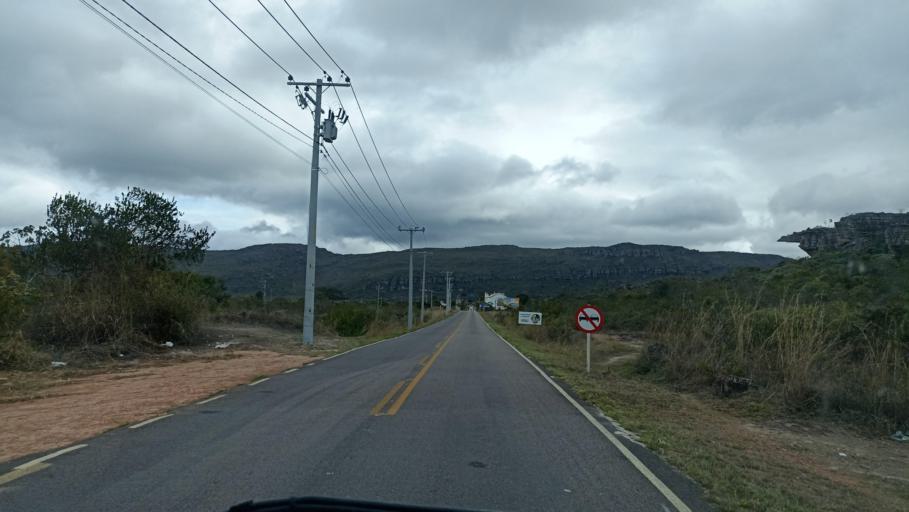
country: BR
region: Bahia
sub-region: Andarai
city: Vera Cruz
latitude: -13.0001
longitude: -41.3634
